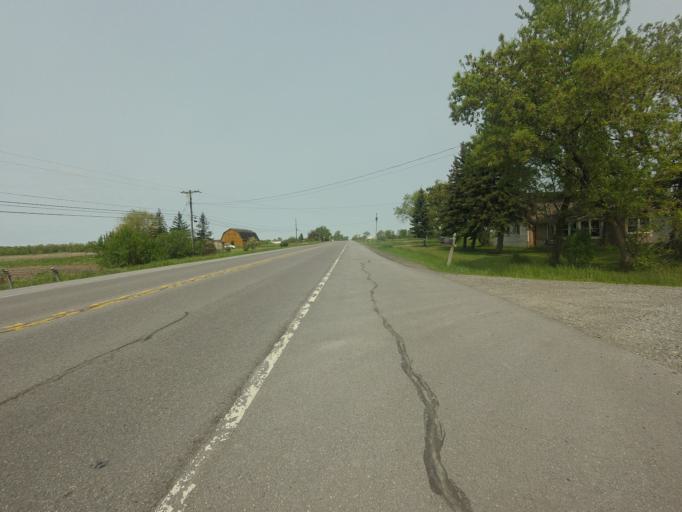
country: US
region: New York
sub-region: Jefferson County
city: Dexter
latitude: 44.0301
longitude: -76.0499
